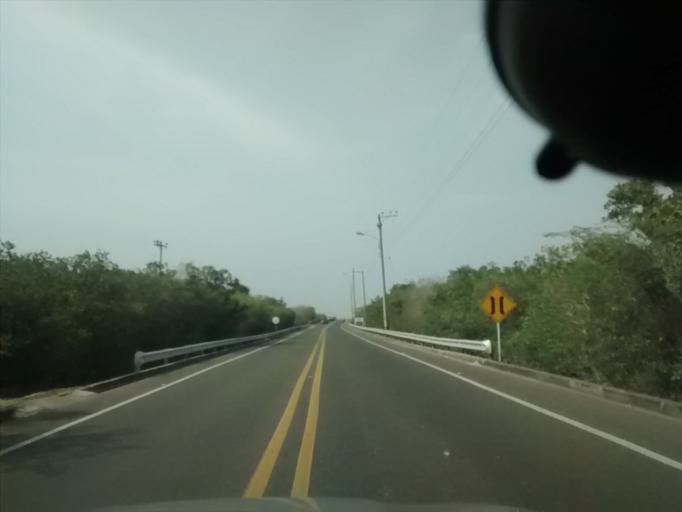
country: CO
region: Bolivar
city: Cartagena
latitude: 10.4872
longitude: -75.4847
